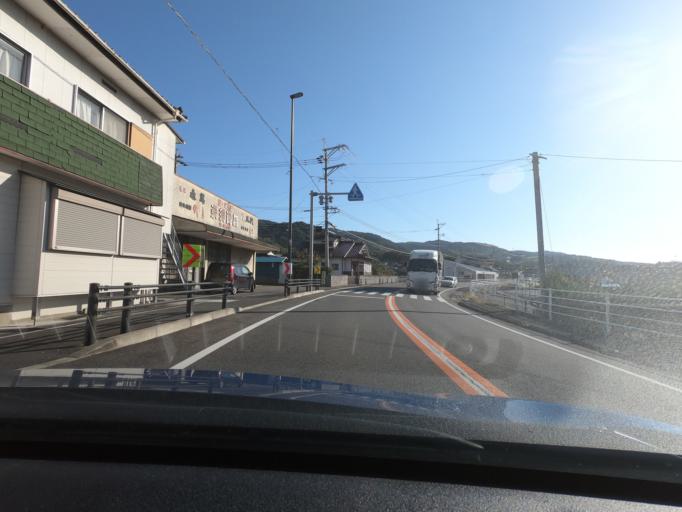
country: JP
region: Kumamoto
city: Minamata
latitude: 32.1772
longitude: 130.3838
